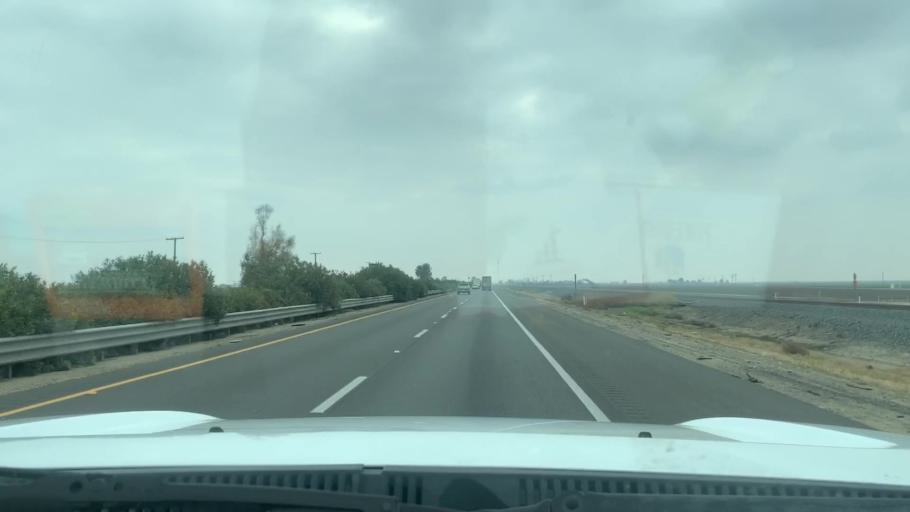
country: US
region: California
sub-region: Tulare County
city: Tipton
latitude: 36.0873
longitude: -119.3208
